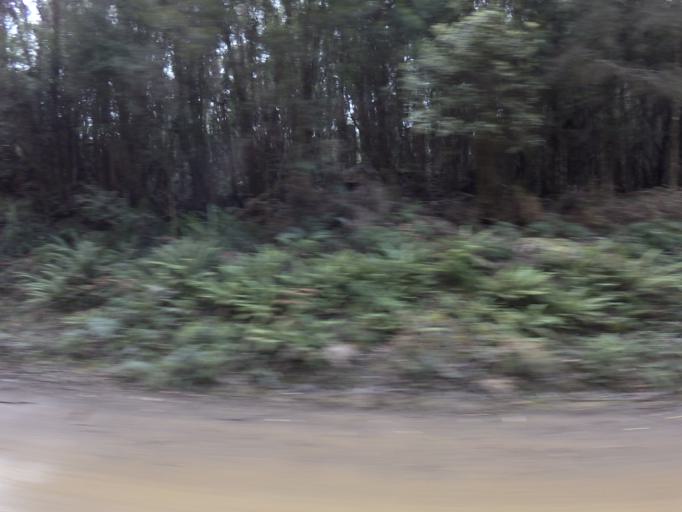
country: AU
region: Tasmania
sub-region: Huon Valley
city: Geeveston
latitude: -43.4069
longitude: 146.8689
